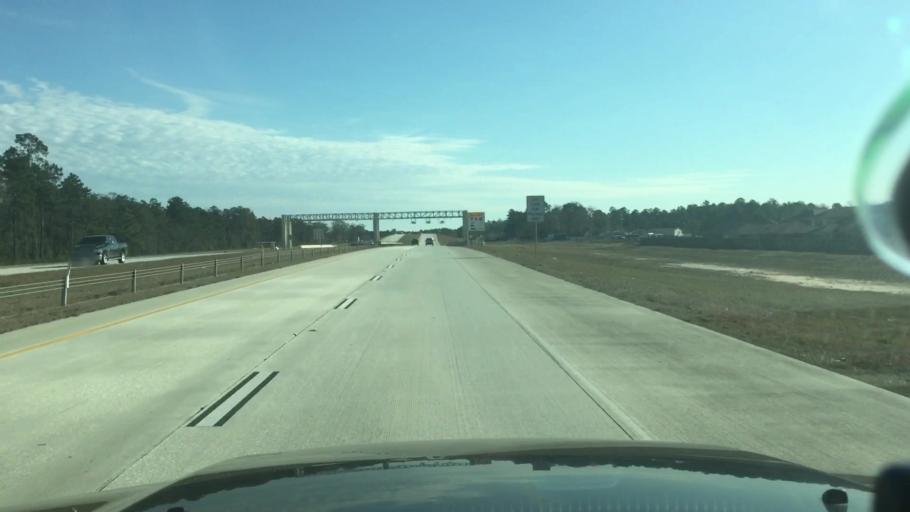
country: US
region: Texas
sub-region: Montgomery County
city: Porter Heights
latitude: 30.1376
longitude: -95.2805
